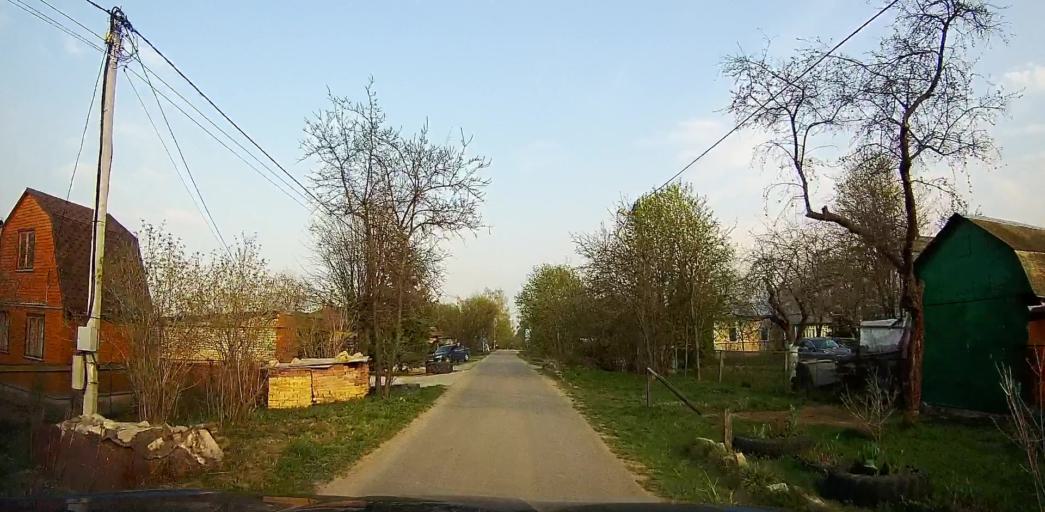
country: RU
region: Moskovskaya
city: Andreyevskoye
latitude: 55.5501
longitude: 37.9532
